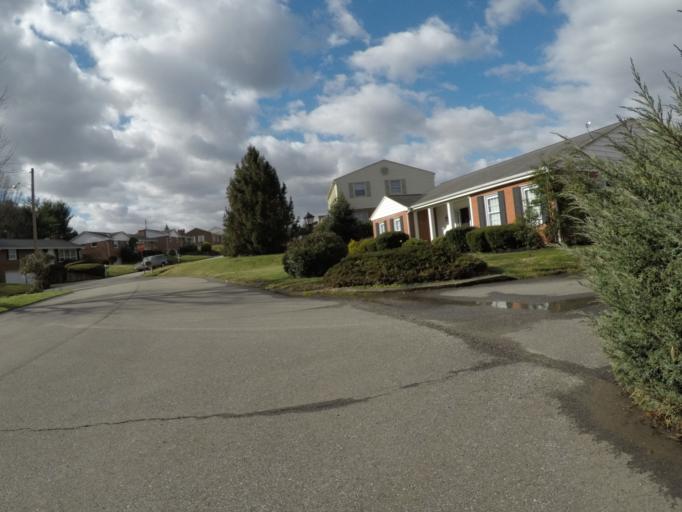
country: US
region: West Virginia
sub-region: Cabell County
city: Huntington
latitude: 38.4097
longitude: -82.3862
